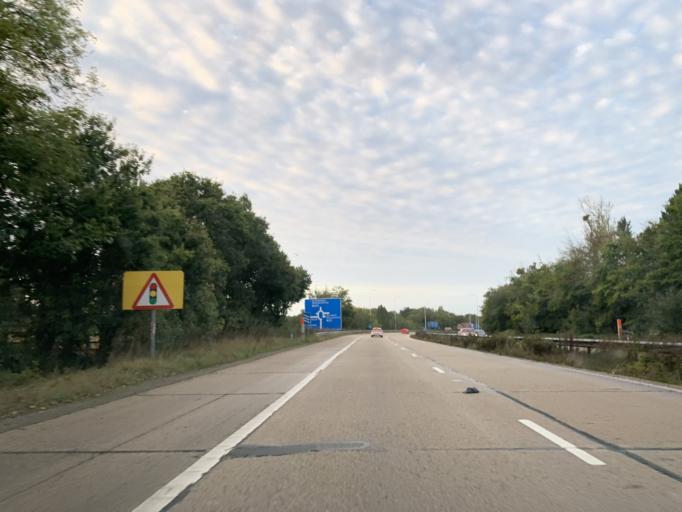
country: GB
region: England
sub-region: Hampshire
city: Totton
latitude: 50.9495
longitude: -1.4754
